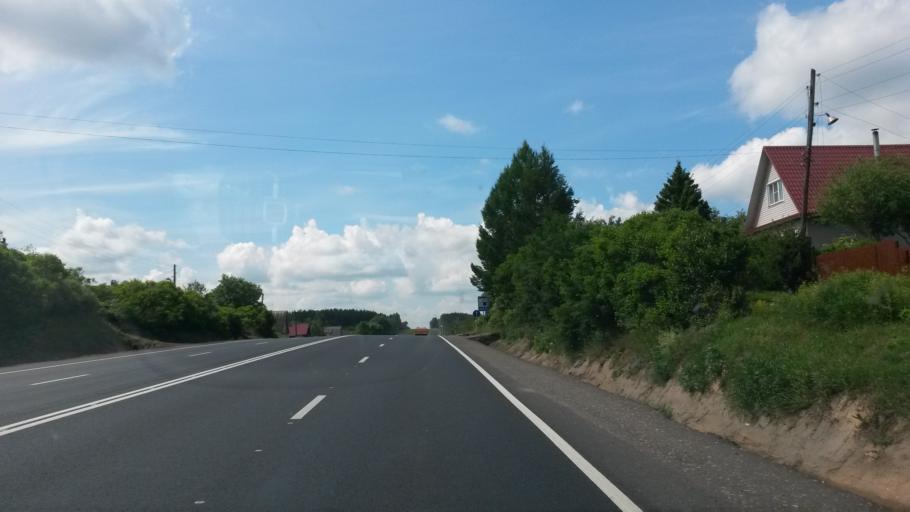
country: RU
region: Jaroslavl
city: Petrovsk
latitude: 56.8862
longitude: 39.0922
